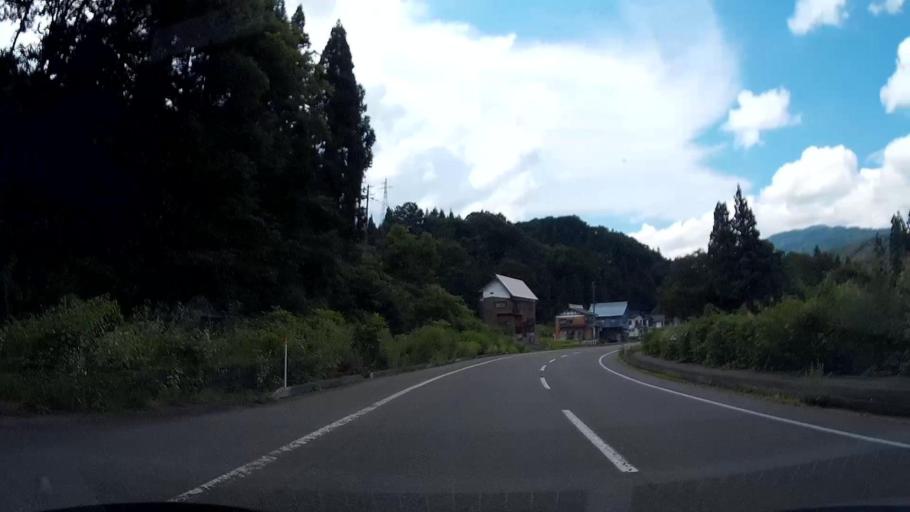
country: JP
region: Niigata
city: Tokamachi
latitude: 36.9924
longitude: 138.6086
